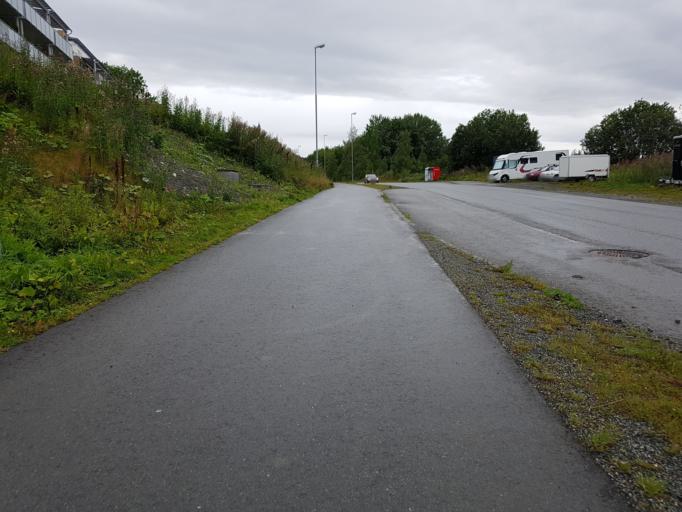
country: NO
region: Sor-Trondelag
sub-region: Trondheim
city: Trondheim
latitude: 63.4091
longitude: 10.4805
